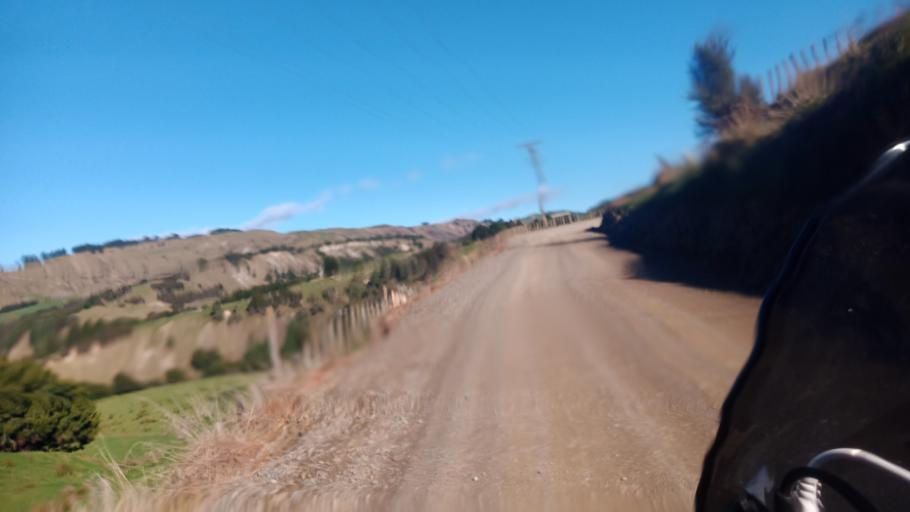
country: NZ
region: Hawke's Bay
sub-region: Wairoa District
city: Wairoa
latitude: -38.8123
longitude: 177.2892
